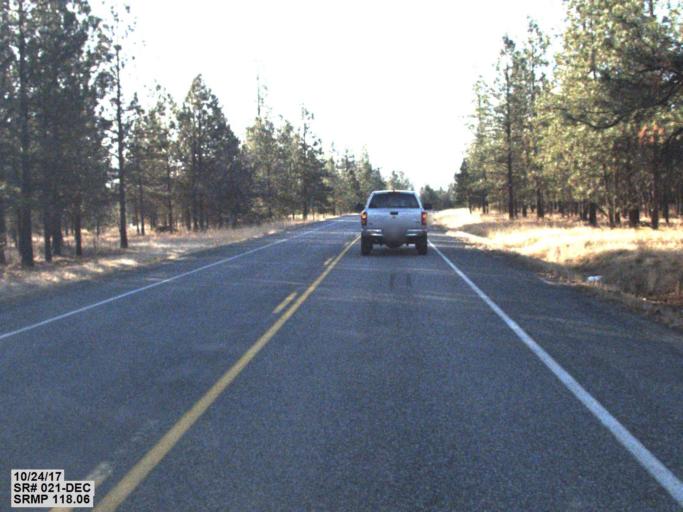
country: US
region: Washington
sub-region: Okanogan County
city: Coulee Dam
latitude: 48.0956
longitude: -118.6929
